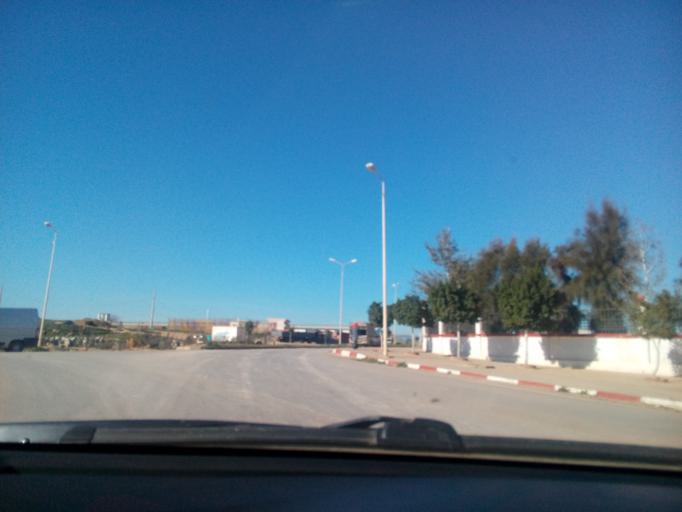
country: DZ
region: Relizane
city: Relizane
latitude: 35.7196
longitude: 0.5291
